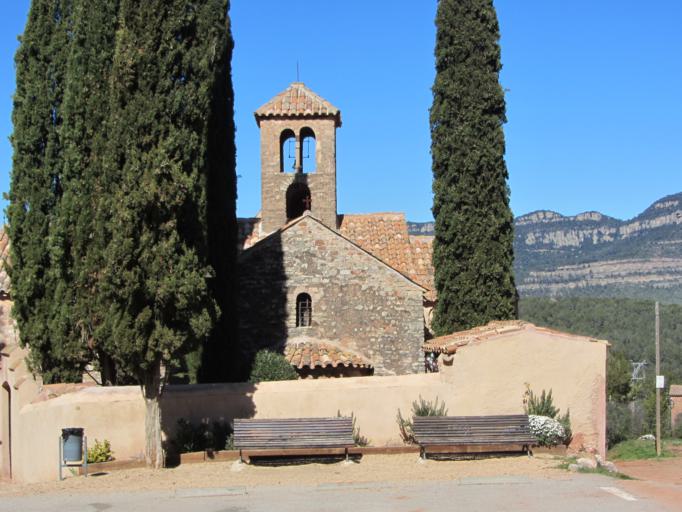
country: ES
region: Catalonia
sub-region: Provincia de Barcelona
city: Gallifa
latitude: 41.6641
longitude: 2.1190
